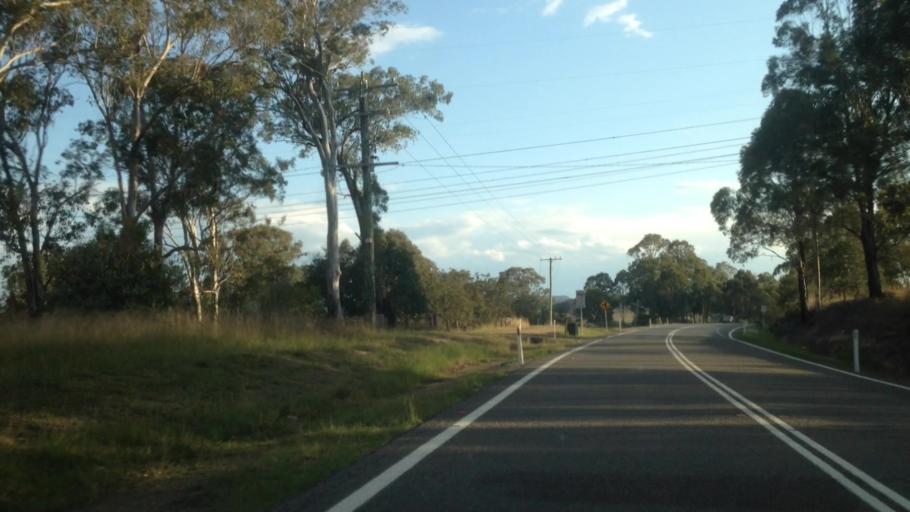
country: AU
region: New South Wales
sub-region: Cessnock
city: Kurri Kurri
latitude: -32.8703
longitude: 151.4791
